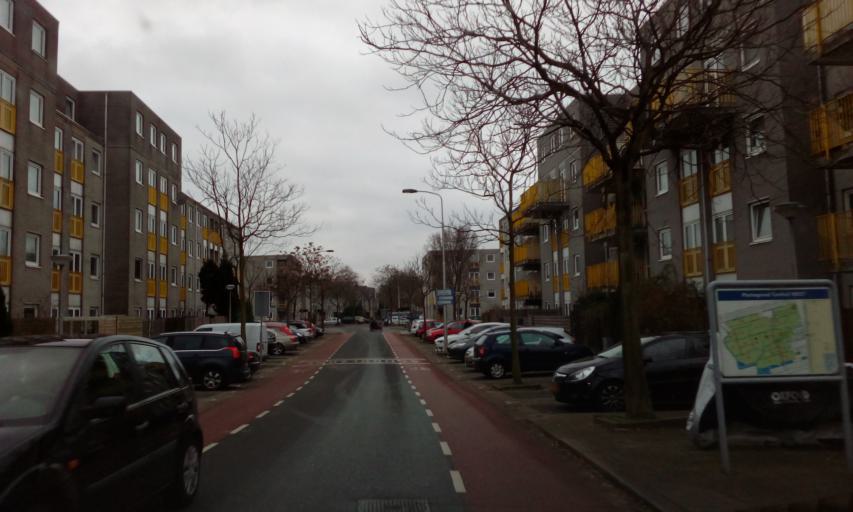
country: NL
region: South Holland
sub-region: Gemeente Delft
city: Delft
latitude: 51.9812
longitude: 4.3473
